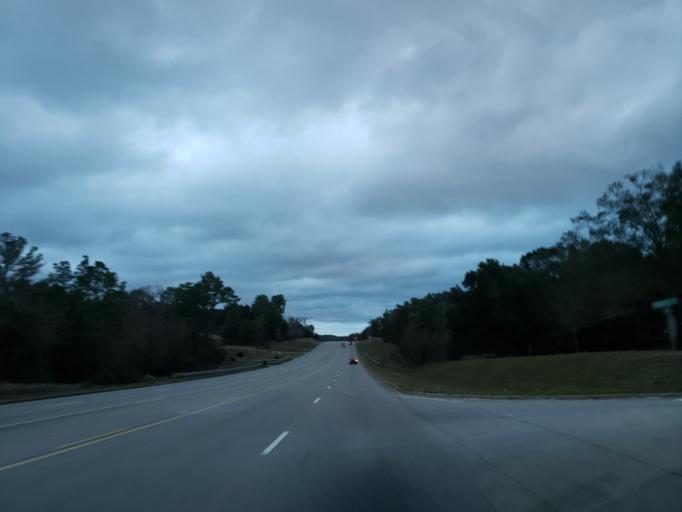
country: US
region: Alabama
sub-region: Mobile County
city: Chickasaw
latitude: 30.7976
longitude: -88.2254
